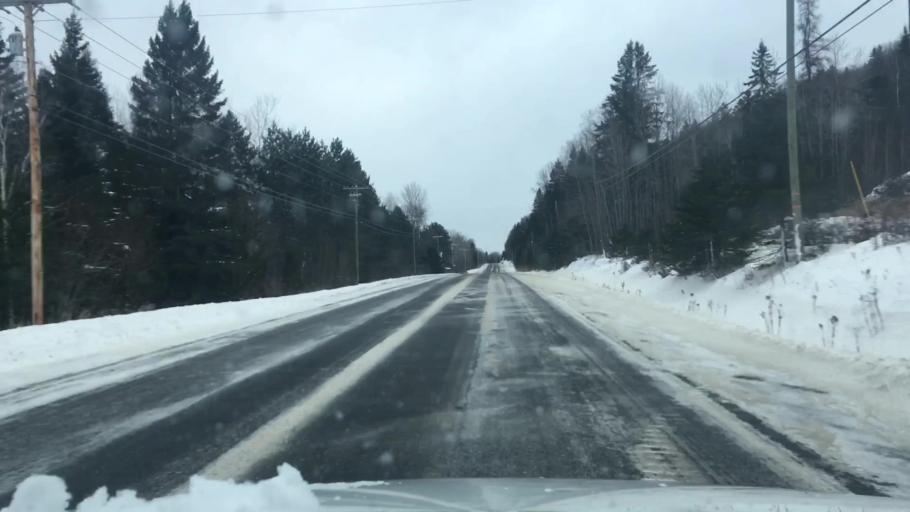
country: US
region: Maine
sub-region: Aroostook County
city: Madawaska
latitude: 47.3305
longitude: -68.1977
